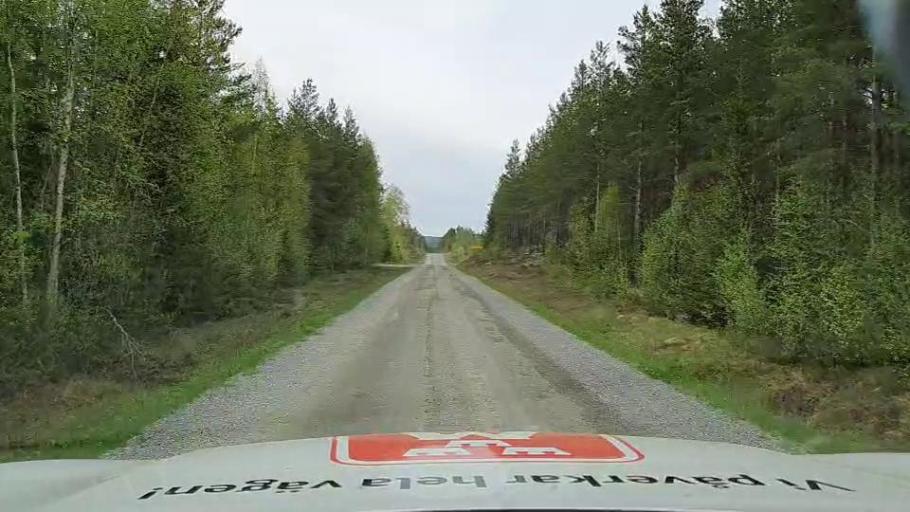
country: SE
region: Jaemtland
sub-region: Braecke Kommun
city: Braecke
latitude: 62.4719
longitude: 14.9160
